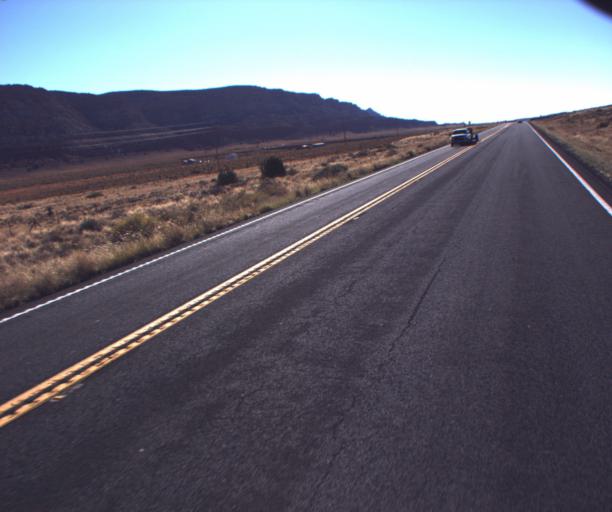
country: US
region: Arizona
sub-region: Coconino County
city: Tuba City
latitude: 36.4436
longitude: -111.5560
